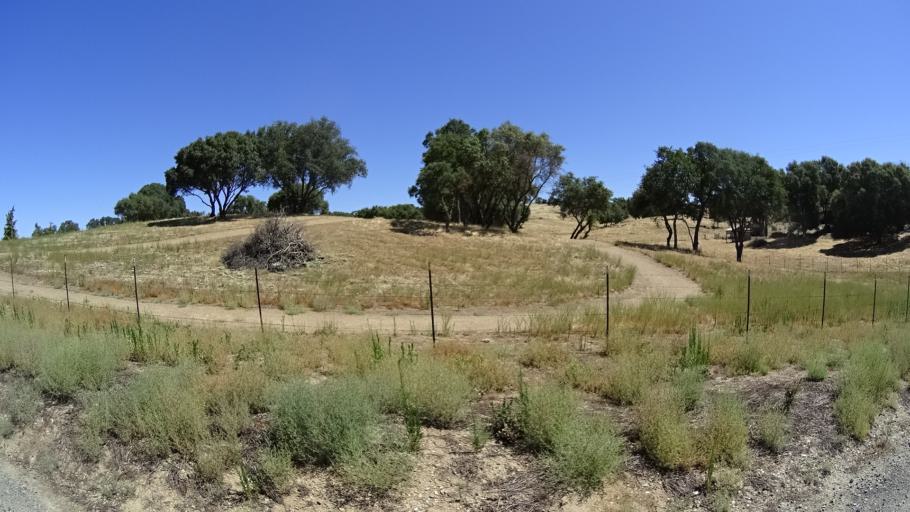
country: US
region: California
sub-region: Calaveras County
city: Copperopolis
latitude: 37.9506
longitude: -120.6814
